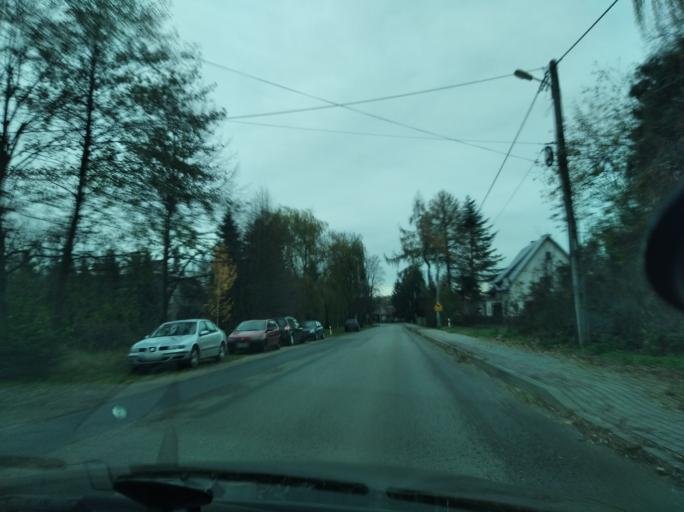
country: PL
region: Subcarpathian Voivodeship
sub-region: Powiat lancucki
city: Krzemienica
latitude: 50.0811
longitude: 22.1894
